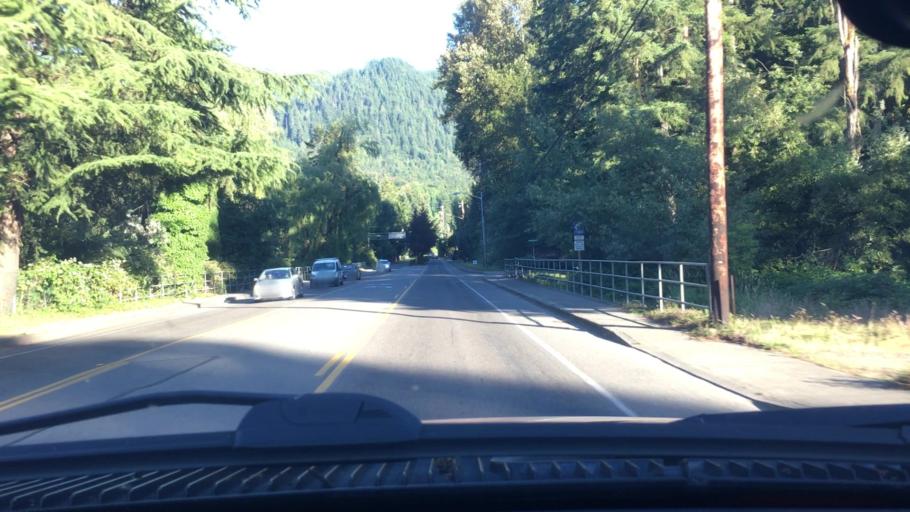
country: US
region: Washington
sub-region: King County
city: Issaquah
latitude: 47.5182
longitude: -122.0293
